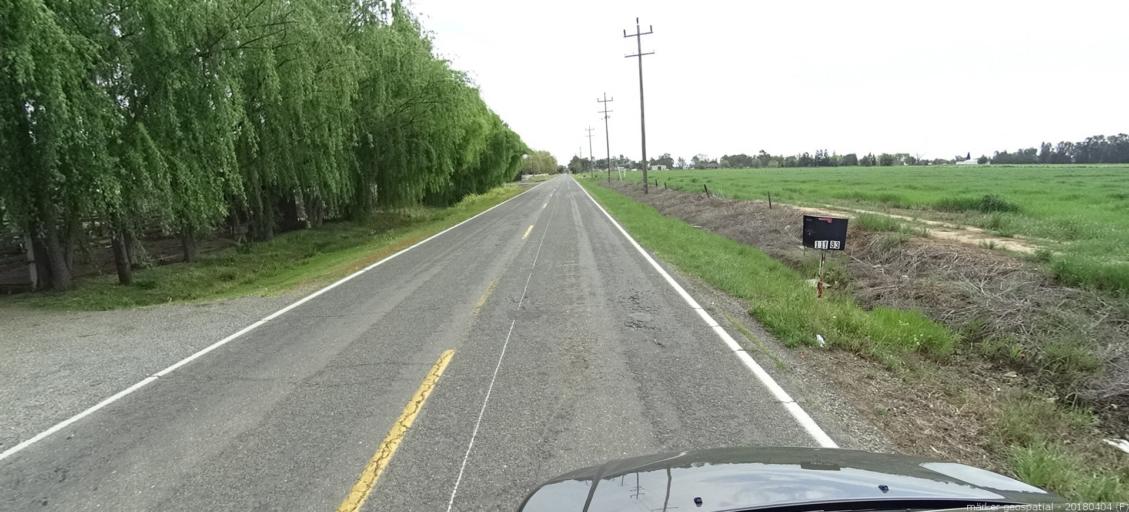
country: US
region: California
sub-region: Sacramento County
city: Galt
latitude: 38.2624
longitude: -121.2700
